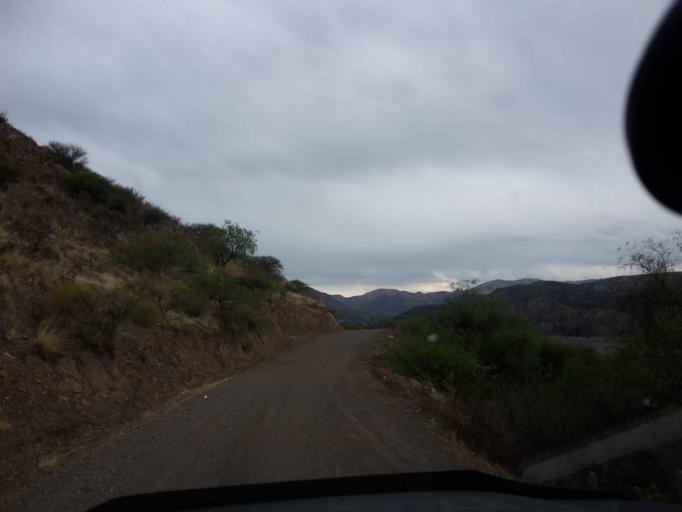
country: BO
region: Cochabamba
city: Sipe Sipe
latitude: -17.5291
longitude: -66.5224
